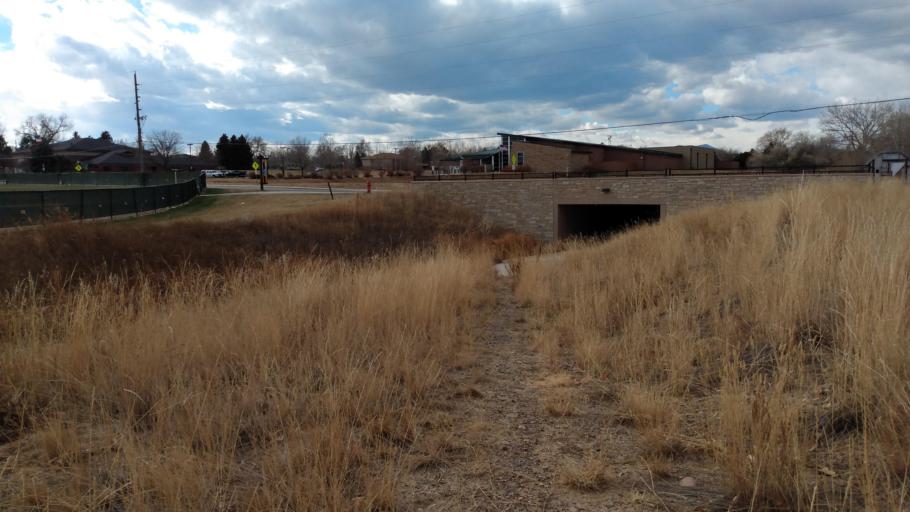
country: US
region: Colorado
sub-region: Boulder County
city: Lafayette
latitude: 40.0032
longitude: -105.0928
